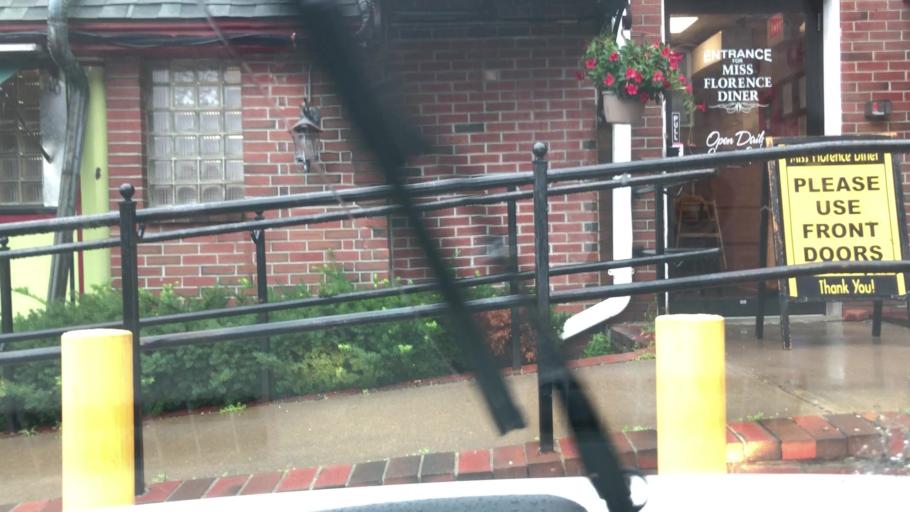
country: US
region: Massachusetts
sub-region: Hampshire County
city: Northampton
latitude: 42.3356
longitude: -72.6713
